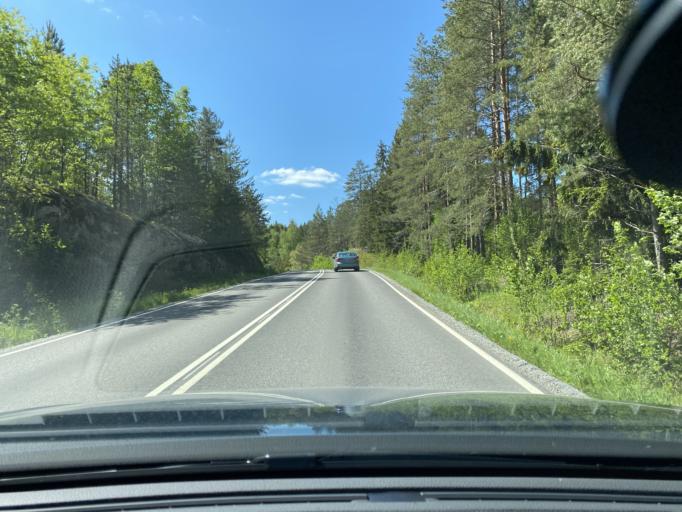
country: FI
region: Varsinais-Suomi
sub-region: Salo
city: Halikko
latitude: 60.3364
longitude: 22.9438
